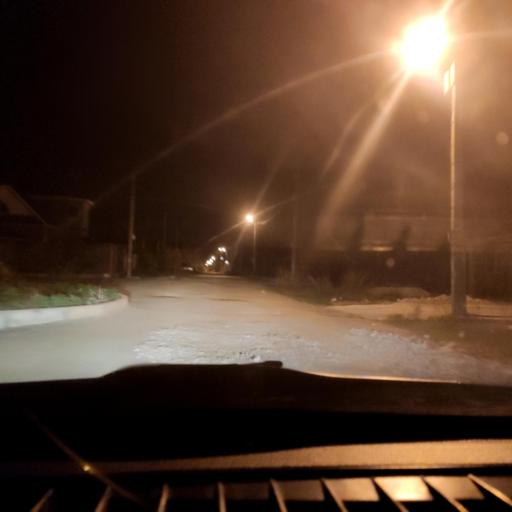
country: RU
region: Samara
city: Podstepki
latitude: 53.5158
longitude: 49.2145
